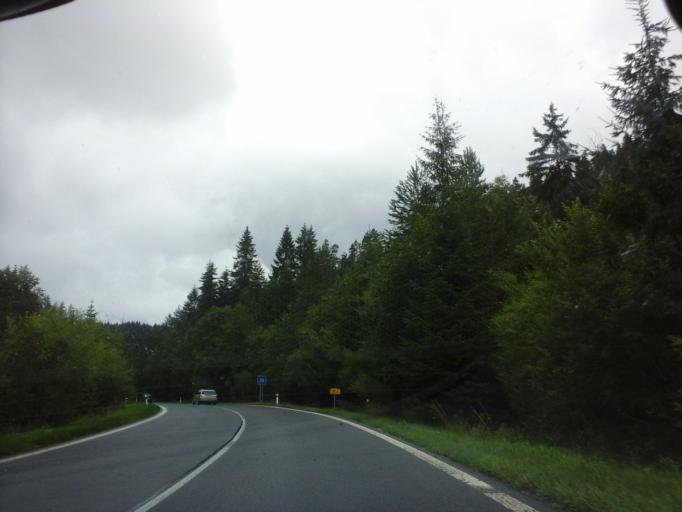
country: SK
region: Kosicky
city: Dobsina
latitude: 48.8810
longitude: 20.2563
